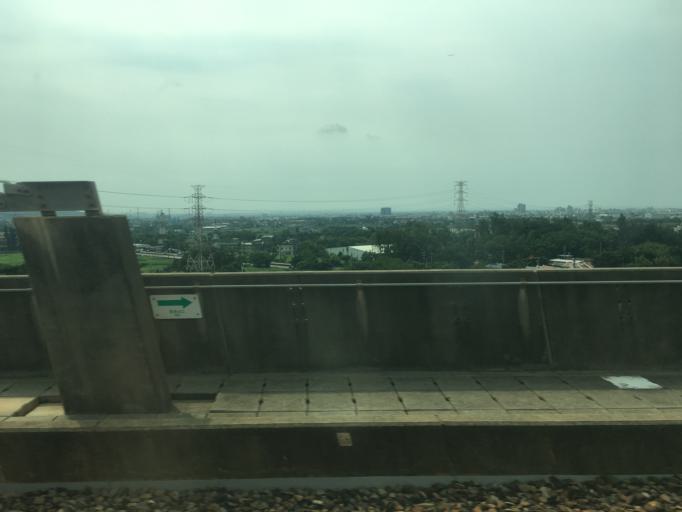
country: TW
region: Taiwan
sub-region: Hsinchu
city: Zhubei
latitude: 24.8791
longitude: 121.0677
